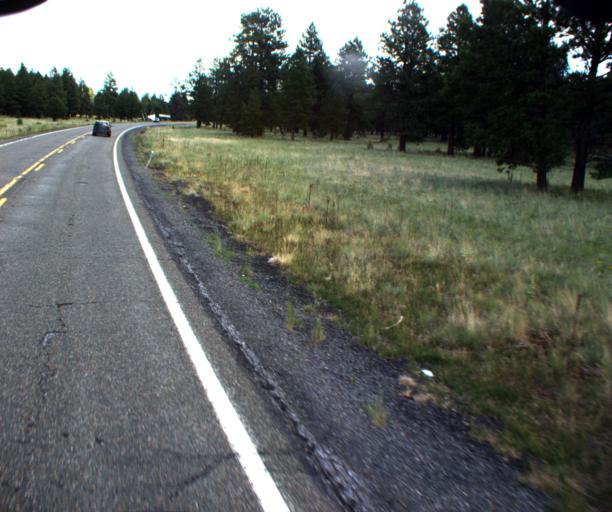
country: US
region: Arizona
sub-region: Coconino County
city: Parks
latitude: 35.3950
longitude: -111.7690
